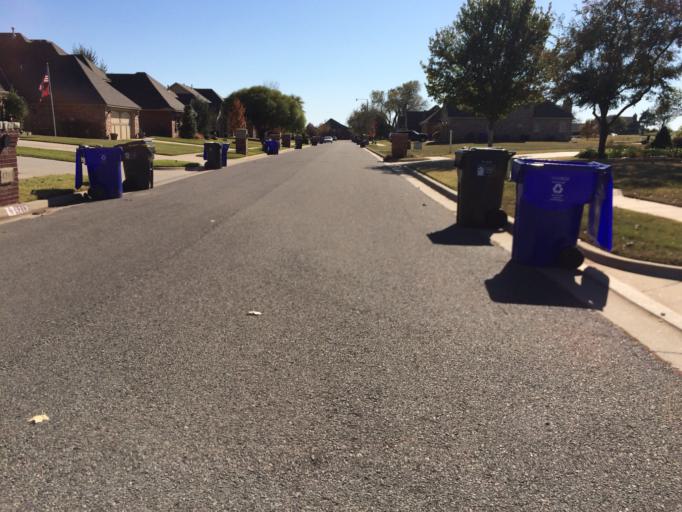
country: US
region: Oklahoma
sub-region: Cleveland County
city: Noble
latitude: 35.1672
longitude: -97.4198
